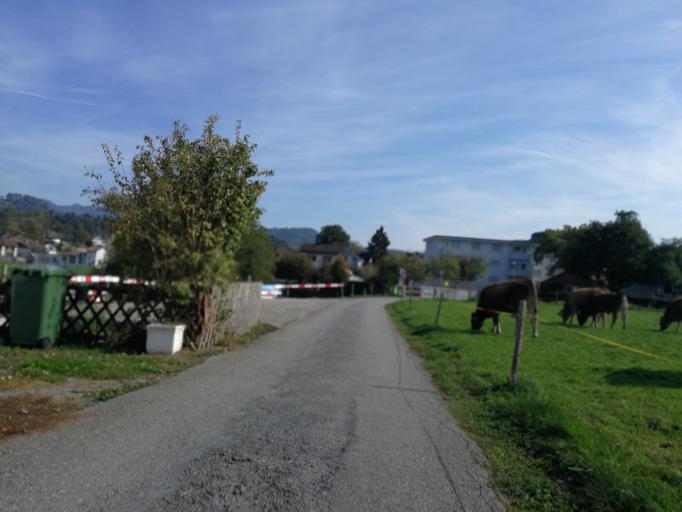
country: CH
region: Zurich
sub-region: Bezirk Hinwil
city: Tann
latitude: 47.2688
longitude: 8.8477
